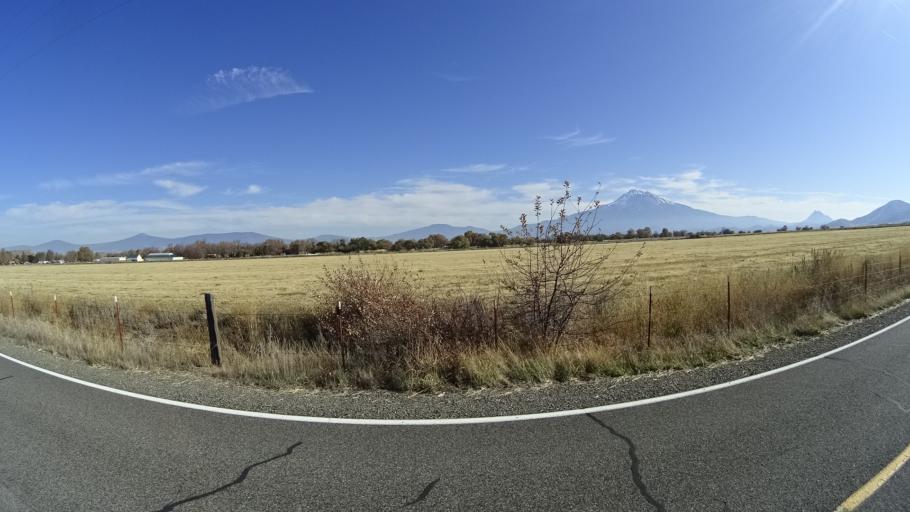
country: US
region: California
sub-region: Siskiyou County
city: Weed
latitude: 41.5154
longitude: -122.5256
